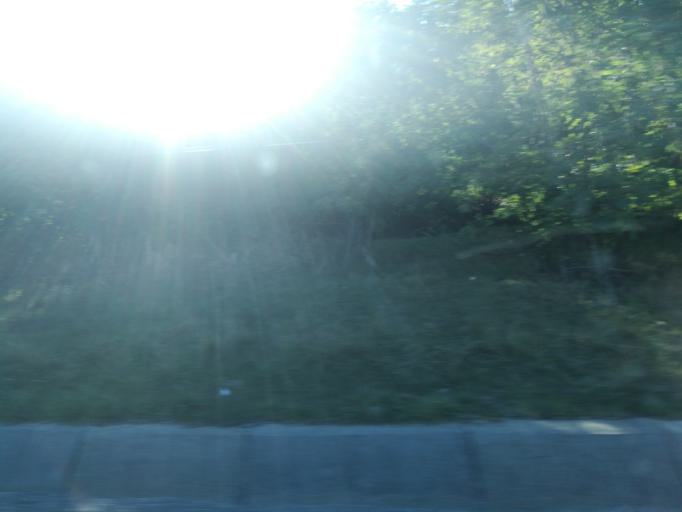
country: RO
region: Brasov
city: Codlea
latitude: 45.7253
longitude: 25.4518
